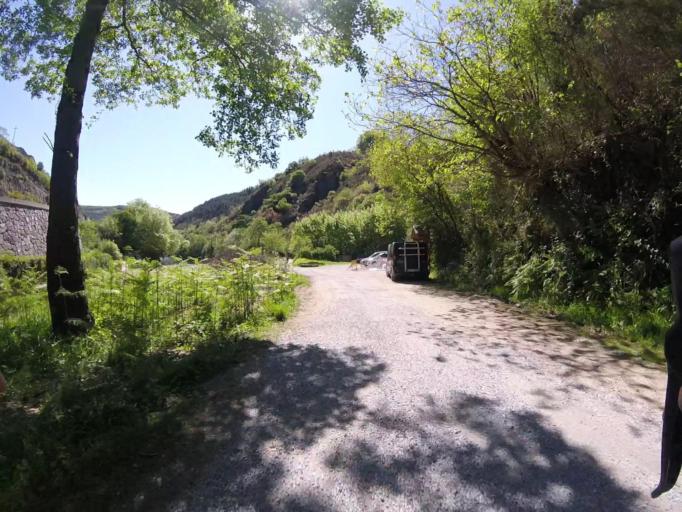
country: ES
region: Navarre
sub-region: Provincia de Navarra
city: Bera
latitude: 43.2918
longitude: -1.7294
